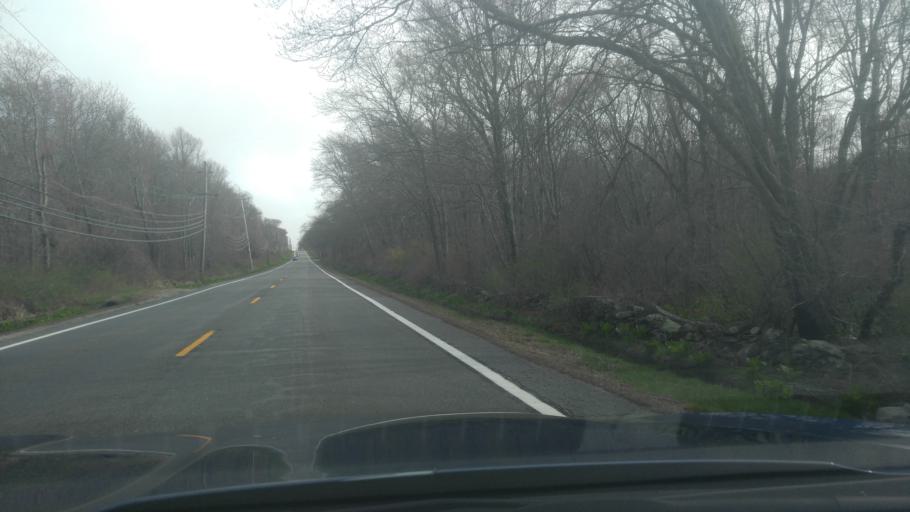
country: US
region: Rhode Island
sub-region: Newport County
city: Jamestown
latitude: 41.5229
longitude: -71.3750
